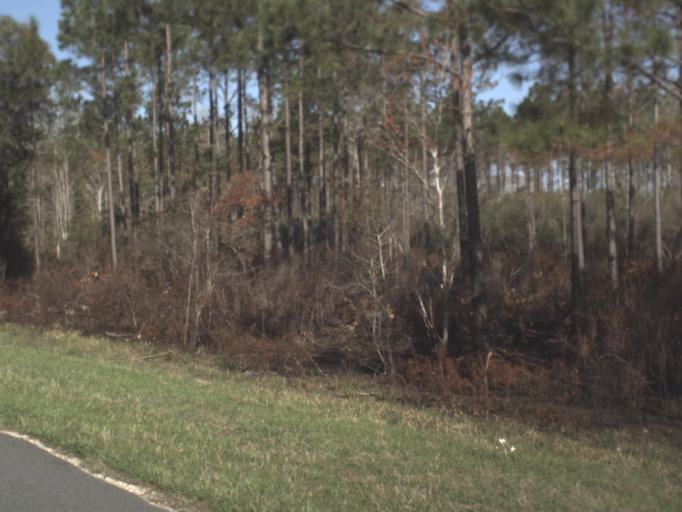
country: US
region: Florida
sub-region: Leon County
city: Woodville
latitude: 30.1879
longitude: -84.0292
